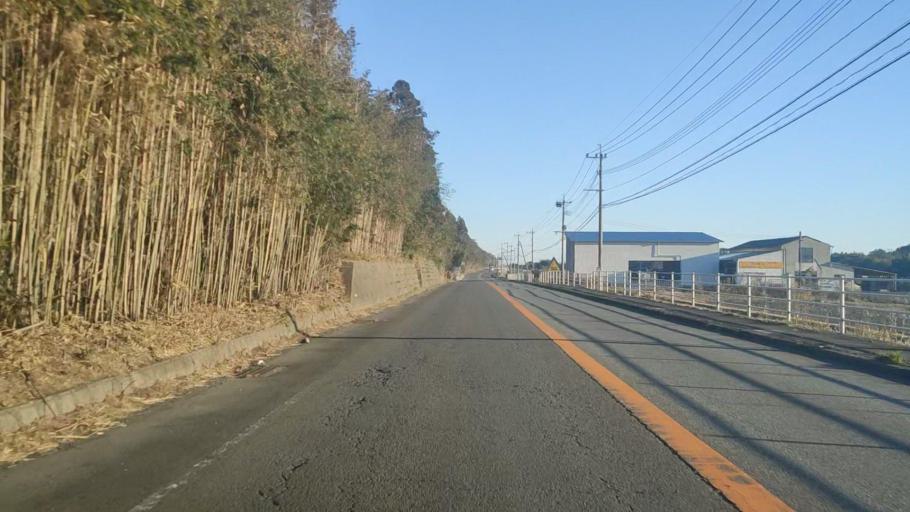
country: JP
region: Miyazaki
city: Takanabe
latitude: 32.0982
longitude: 131.5188
